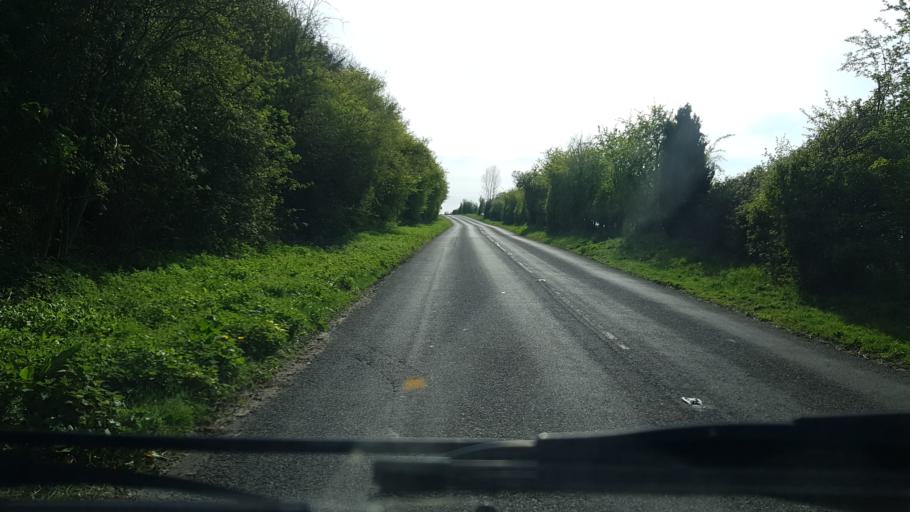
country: GB
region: England
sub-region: Hampshire
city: Kingsclere
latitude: 51.3076
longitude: -1.2574
